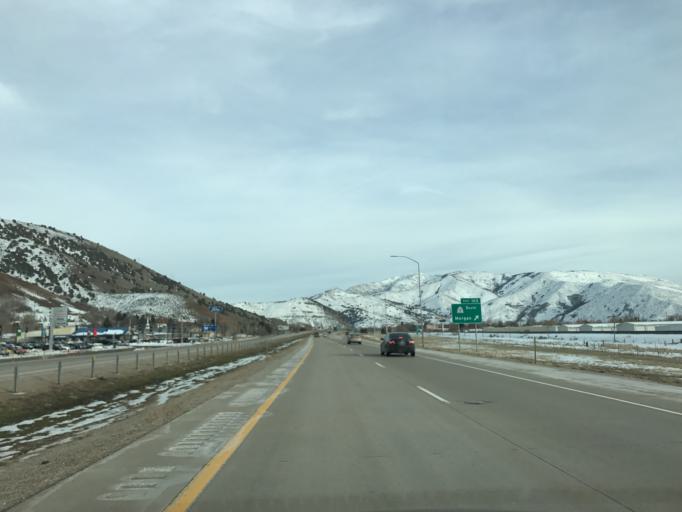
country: US
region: Utah
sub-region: Morgan County
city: Morgan
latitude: 41.0497
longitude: -111.6815
